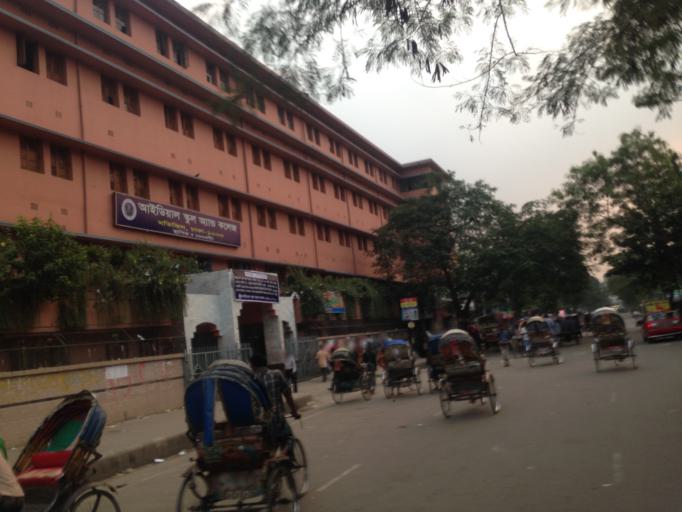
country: BD
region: Dhaka
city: Paltan
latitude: 23.7359
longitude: 90.4227
